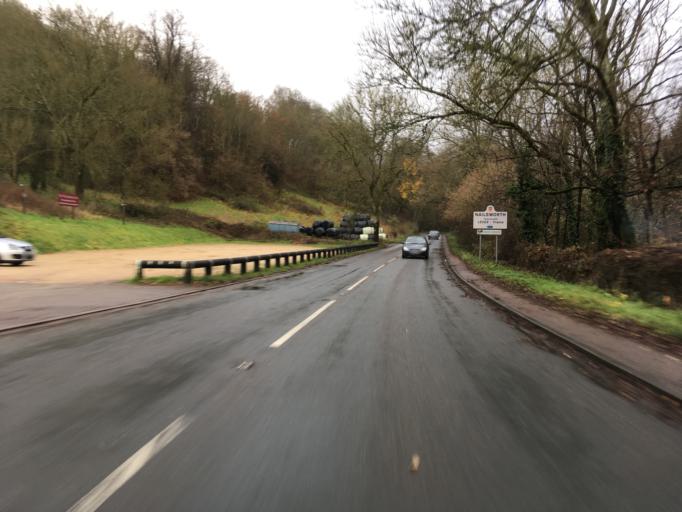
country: GB
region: England
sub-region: Gloucestershire
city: Nailsworth
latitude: 51.6923
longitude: -2.2019
